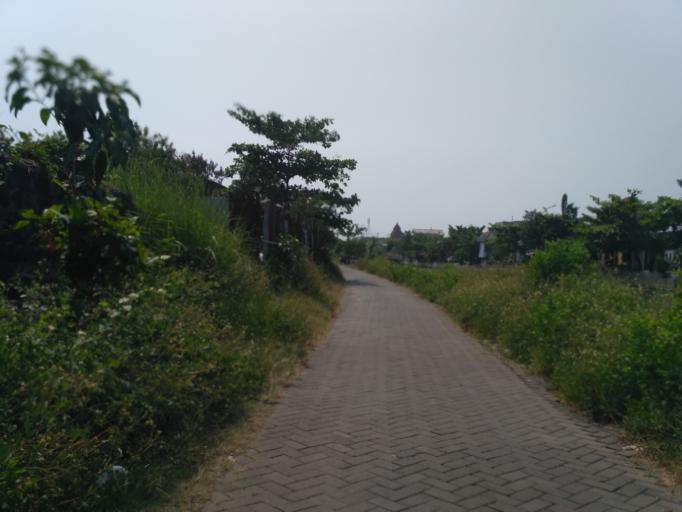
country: ID
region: Central Java
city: Semarang
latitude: -6.9640
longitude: 110.4406
